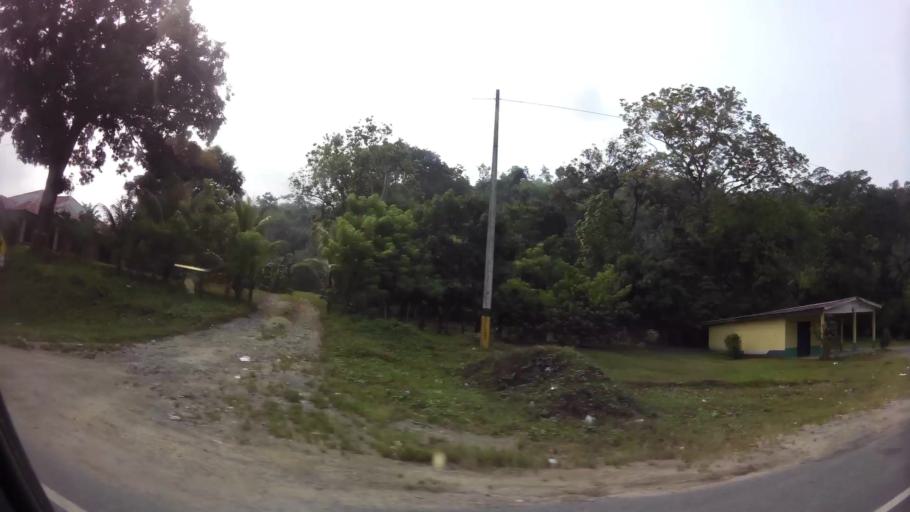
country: HN
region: Yoro
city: Toyos
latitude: 15.5145
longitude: -87.6644
